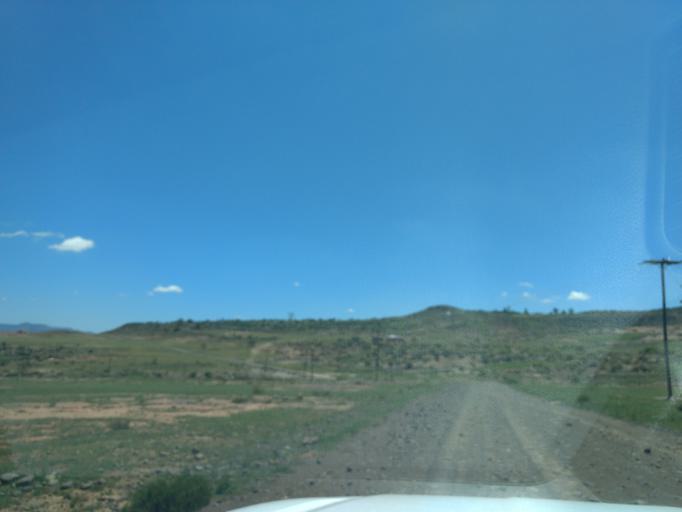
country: LS
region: Maseru
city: Maseru
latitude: -29.4676
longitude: 27.3758
